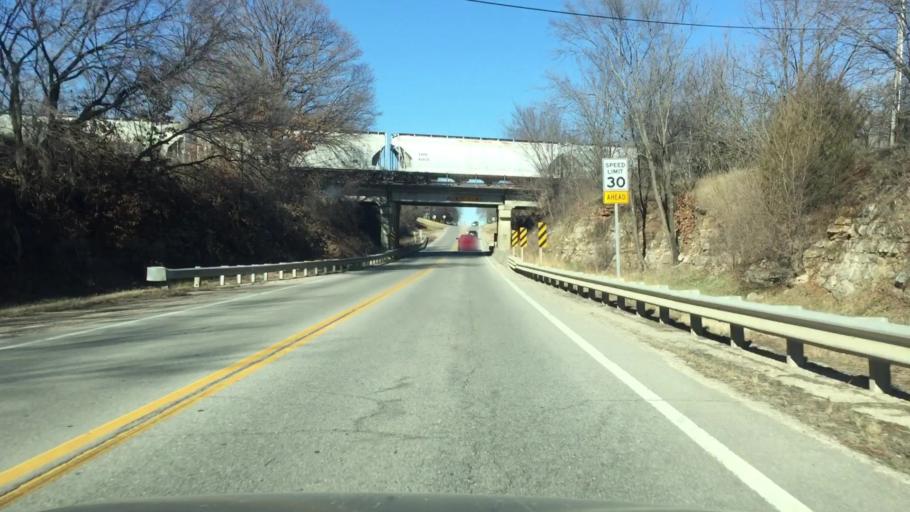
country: US
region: Kansas
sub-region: Anderson County
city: Garnett
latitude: 38.2733
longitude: -95.2492
